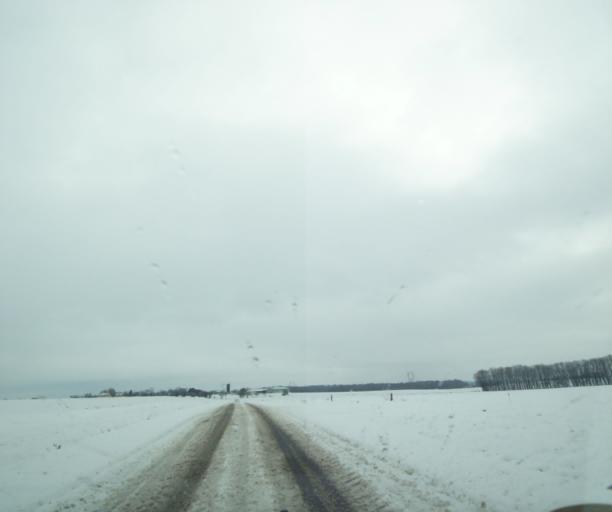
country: FR
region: Champagne-Ardenne
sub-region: Departement de la Haute-Marne
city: Montier-en-Der
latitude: 48.5153
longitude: 4.6818
